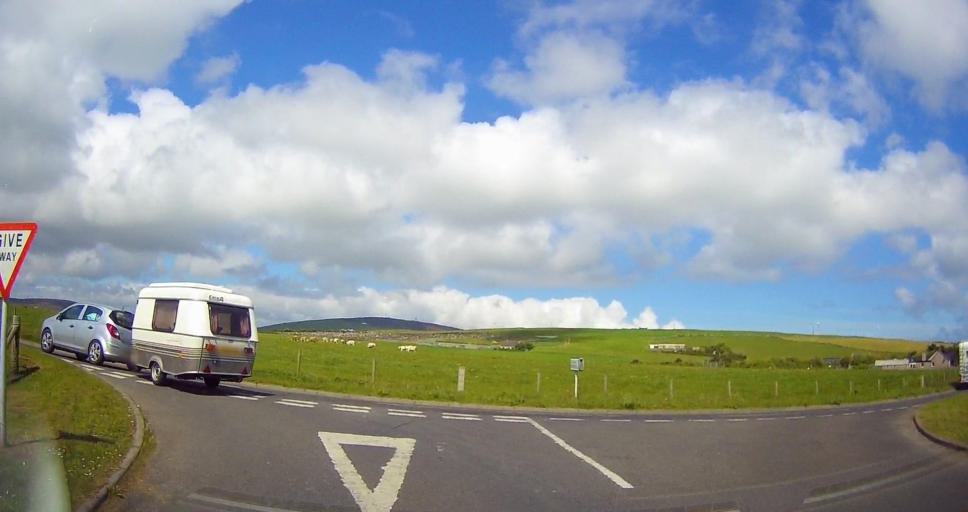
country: GB
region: Scotland
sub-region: Orkney Islands
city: Orkney
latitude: 58.9663
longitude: -2.9773
